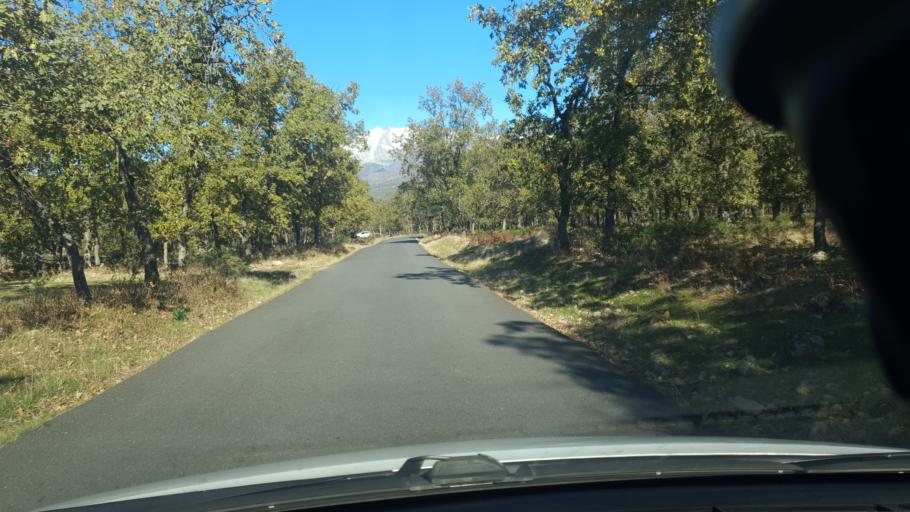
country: ES
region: Castille and Leon
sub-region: Provincia de Avila
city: Candeleda
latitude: 40.1249
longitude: -5.2668
